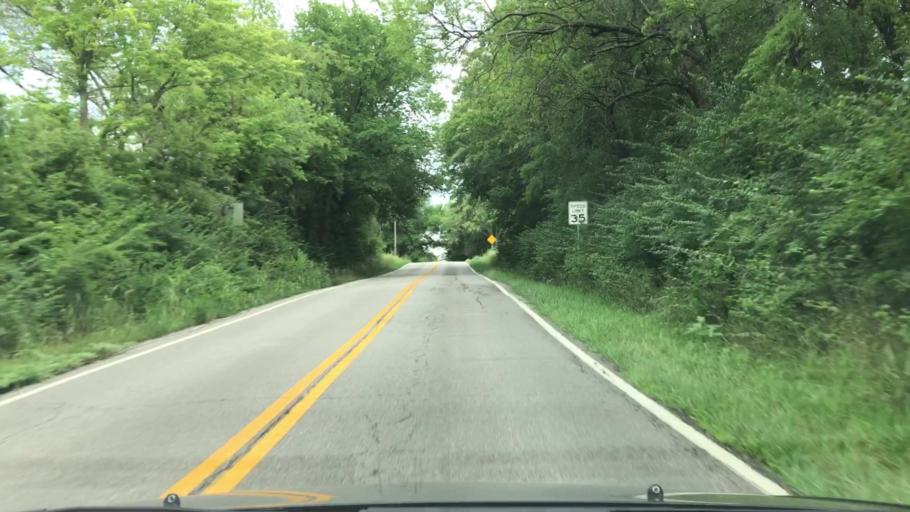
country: US
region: Missouri
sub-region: Jackson County
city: Lees Summit
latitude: 38.8908
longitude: -94.4340
